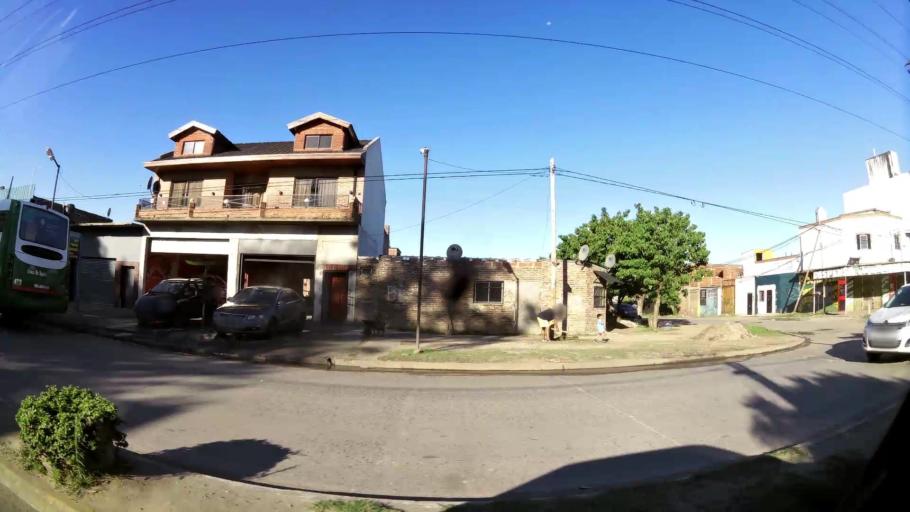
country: AR
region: Buenos Aires
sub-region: Partido de Almirante Brown
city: Adrogue
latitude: -34.7589
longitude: -58.3334
